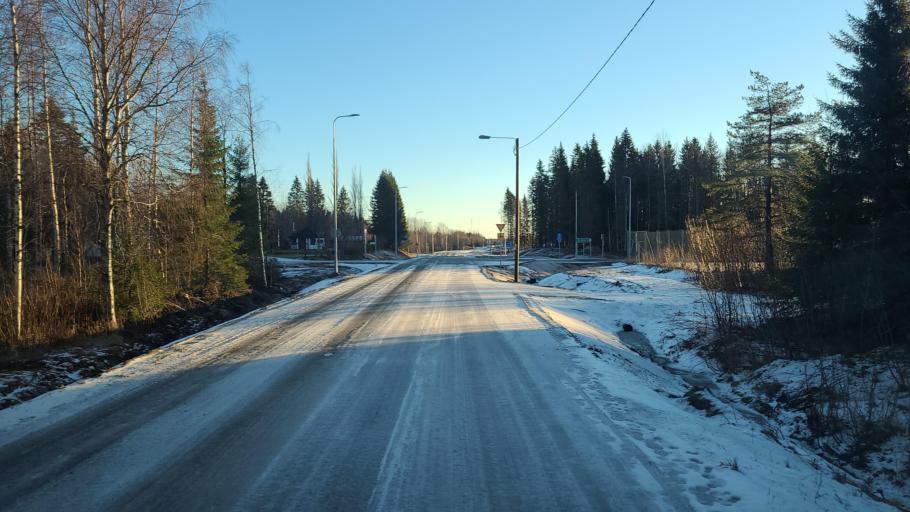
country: FI
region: Lapland
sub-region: Kemi-Tornio
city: Kemi
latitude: 65.6802
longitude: 24.7402
